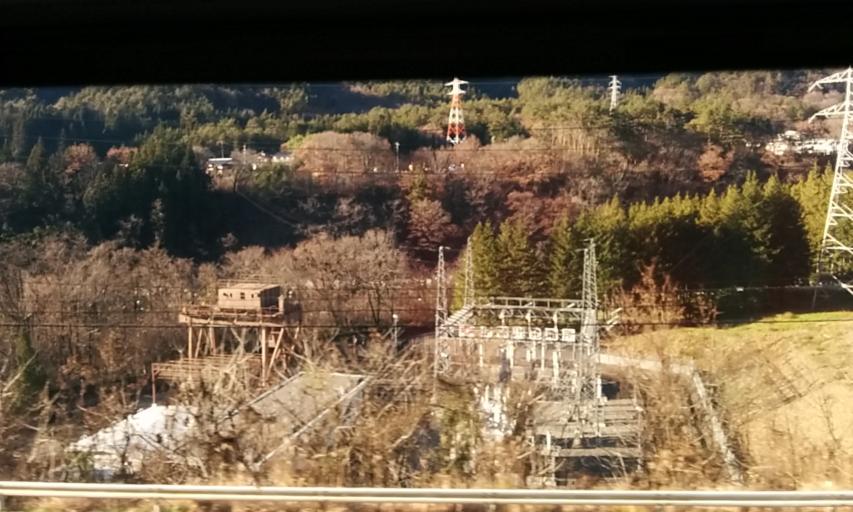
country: JP
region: Nagano
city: Iida
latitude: 35.7042
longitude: 137.7007
